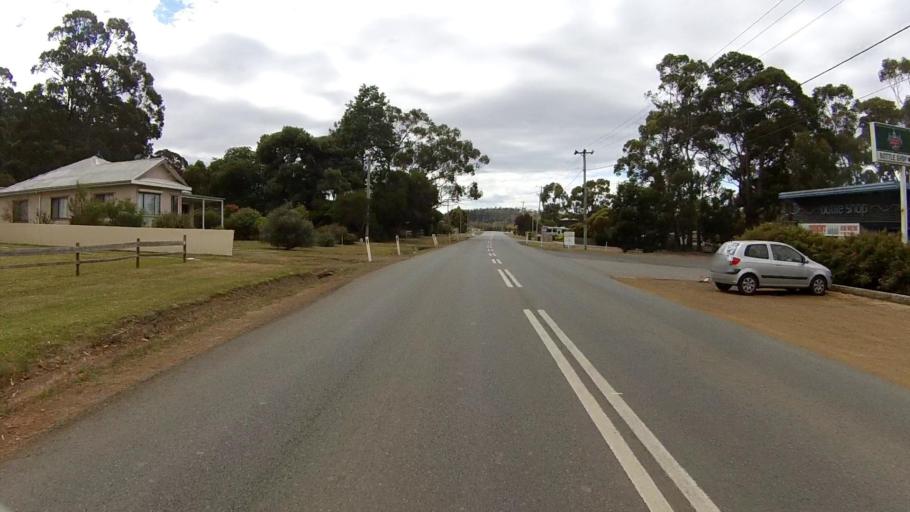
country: AU
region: Tasmania
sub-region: Sorell
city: Sorell
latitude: -42.5538
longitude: 147.8740
